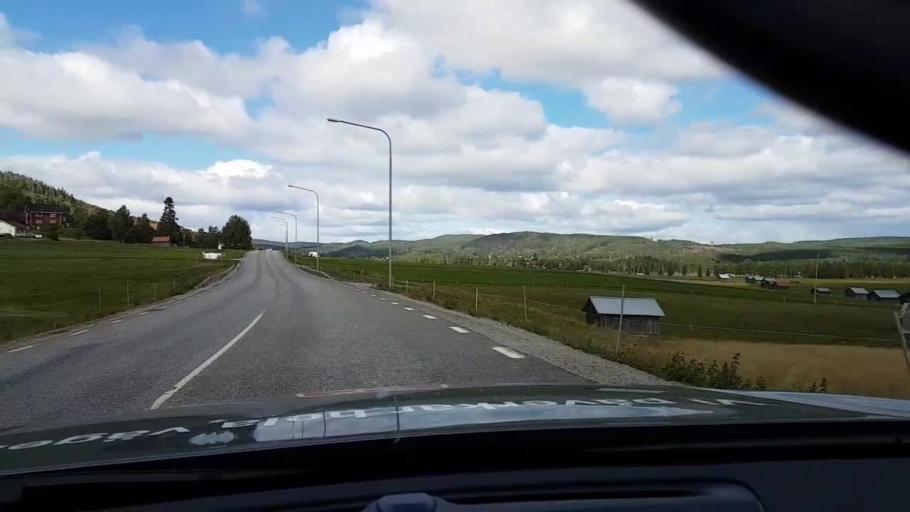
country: SE
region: Vaesternorrland
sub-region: OErnskoeldsviks Kommun
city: Bredbyn
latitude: 63.4983
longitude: 18.0826
